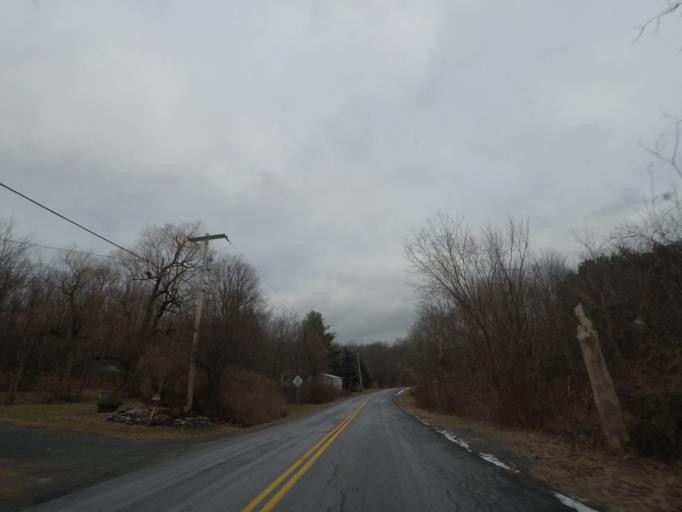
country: US
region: New York
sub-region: Rensselaer County
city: Poestenkill
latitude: 42.7644
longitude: -73.4993
